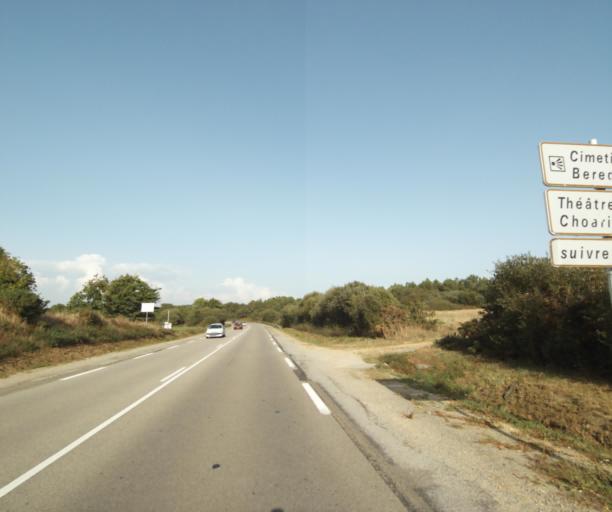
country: FR
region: Brittany
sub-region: Departement du Morbihan
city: Riantec
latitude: 47.7341
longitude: -3.3110
